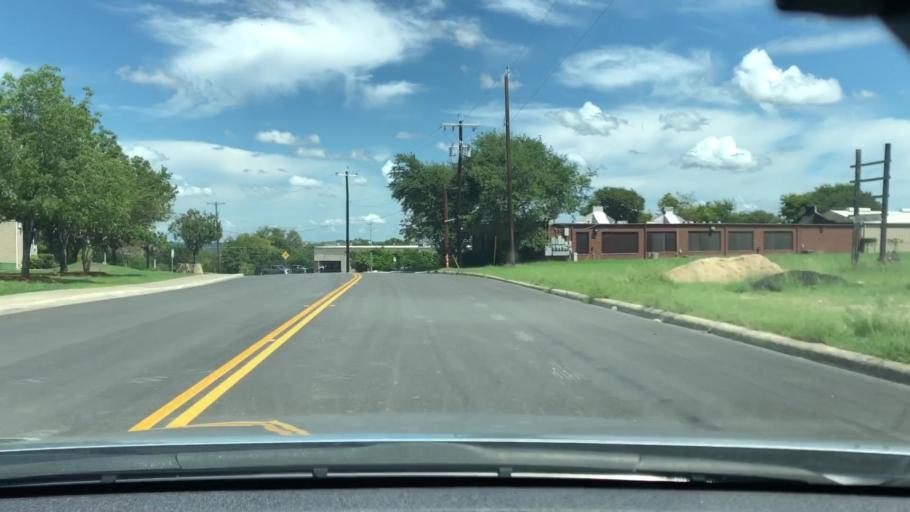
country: US
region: Texas
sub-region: Bexar County
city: Live Oak
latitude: 29.5557
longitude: -98.3200
